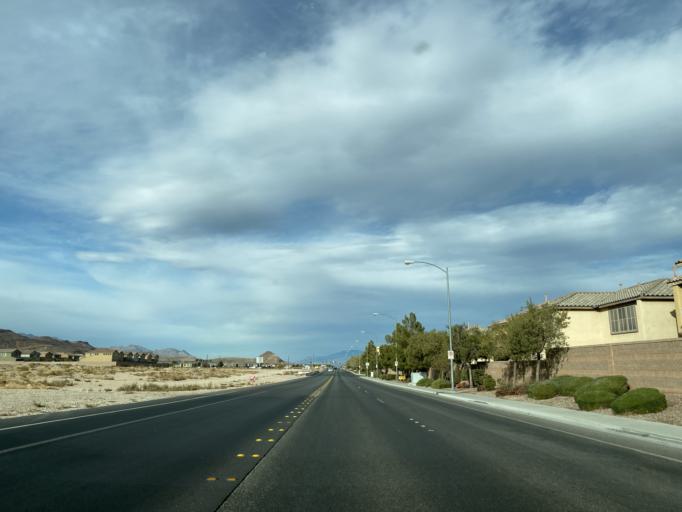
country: US
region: Nevada
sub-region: Clark County
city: Enterprise
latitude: 36.0158
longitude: -115.2980
